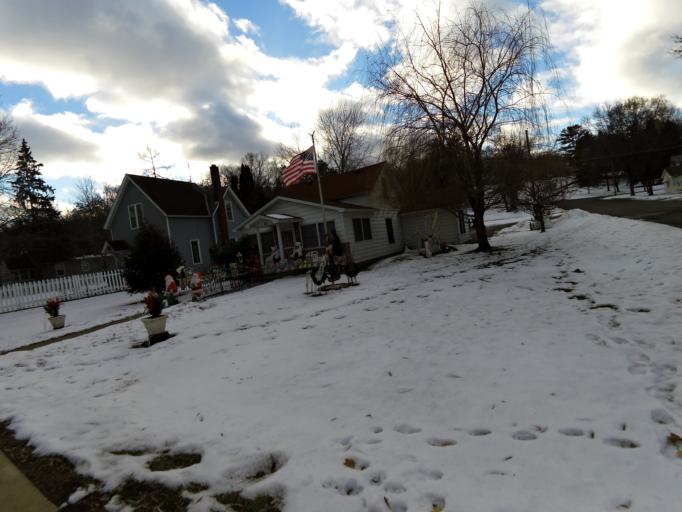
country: US
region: Minnesota
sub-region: Washington County
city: Bayport
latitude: 45.0163
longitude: -92.7825
